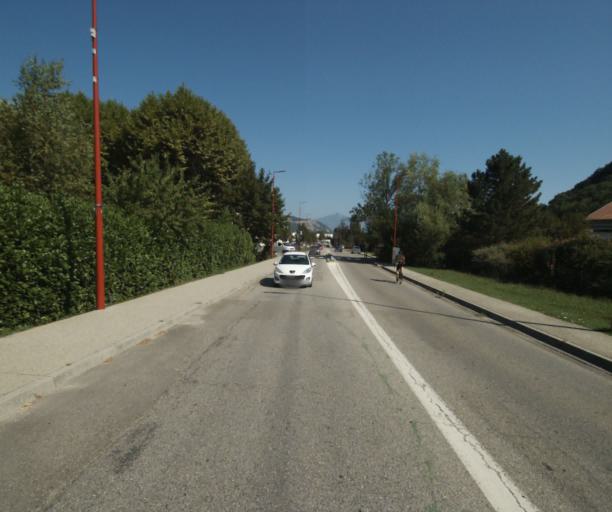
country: FR
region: Rhone-Alpes
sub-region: Departement de l'Isere
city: Allieres-et-Risset
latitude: 45.0942
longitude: 5.6837
